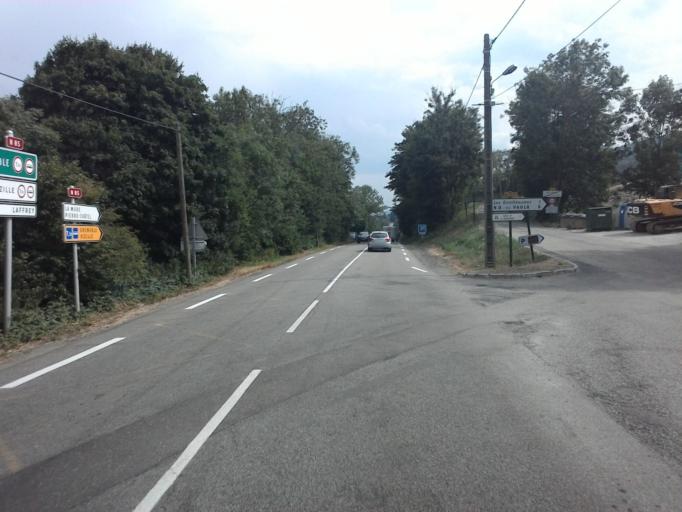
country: FR
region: Rhone-Alpes
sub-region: Departement de l'Isere
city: Pierre-Chatel
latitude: 44.9975
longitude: 5.7730
